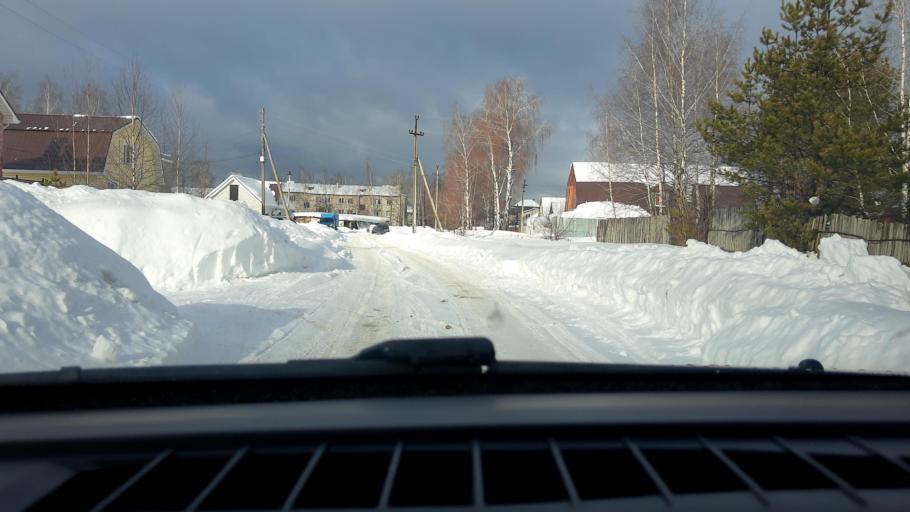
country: RU
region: Nizjnij Novgorod
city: Lukino
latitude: 56.3964
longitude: 43.7069
